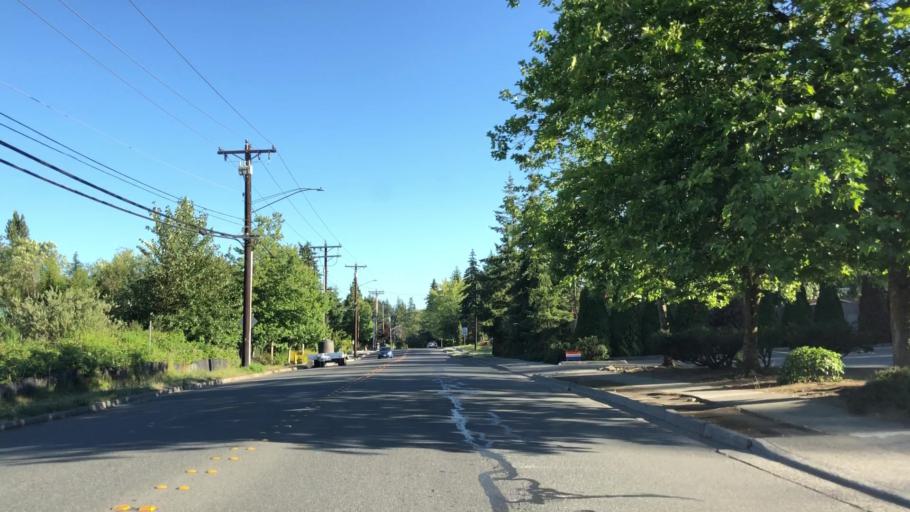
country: US
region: Washington
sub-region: Snohomish County
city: Lynnwood
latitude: 47.8135
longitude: -122.3141
